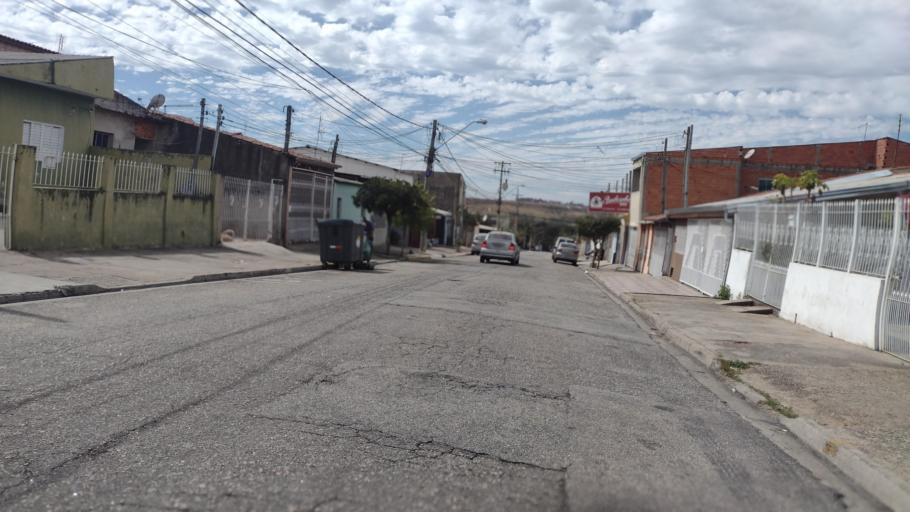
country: BR
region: Sao Paulo
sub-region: Sorocaba
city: Sorocaba
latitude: -23.4311
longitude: -47.4584
